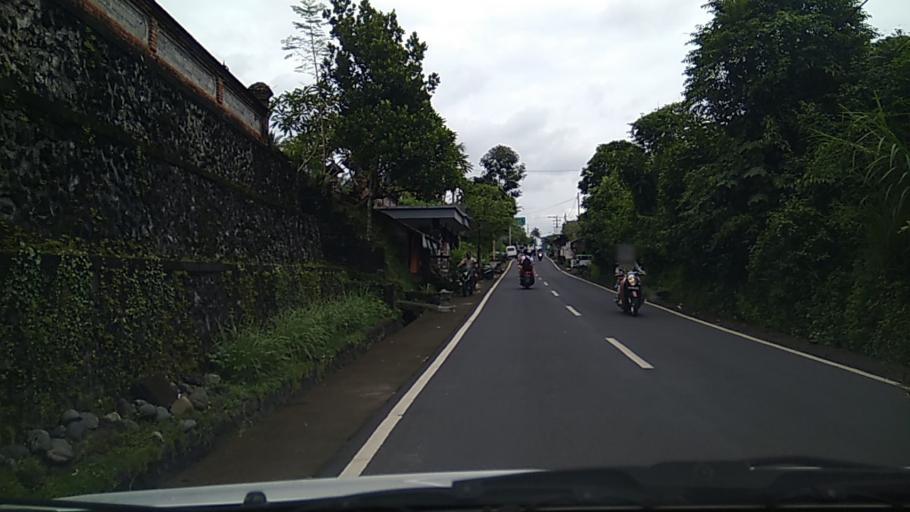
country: ID
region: Bali
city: Banjar Tebongkang
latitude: -8.5265
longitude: 115.2276
